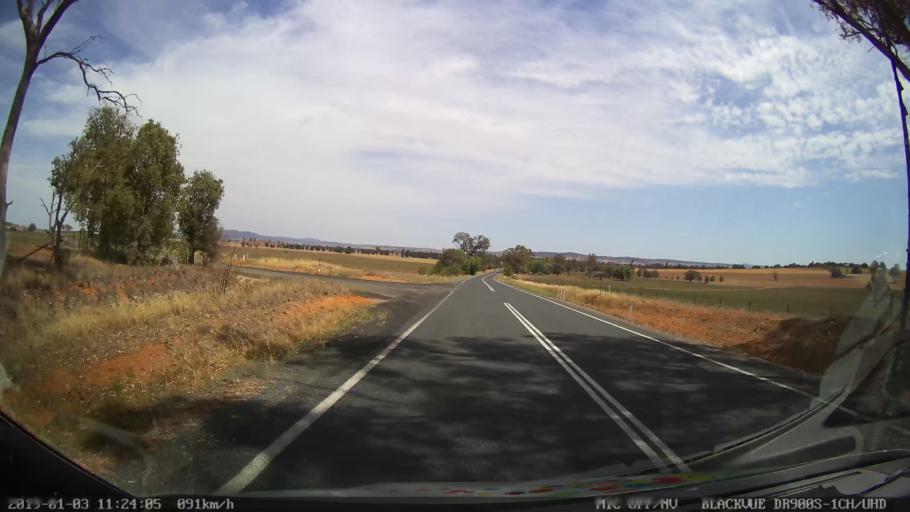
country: AU
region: New South Wales
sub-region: Weddin
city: Grenfell
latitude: -34.0559
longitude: 148.2376
